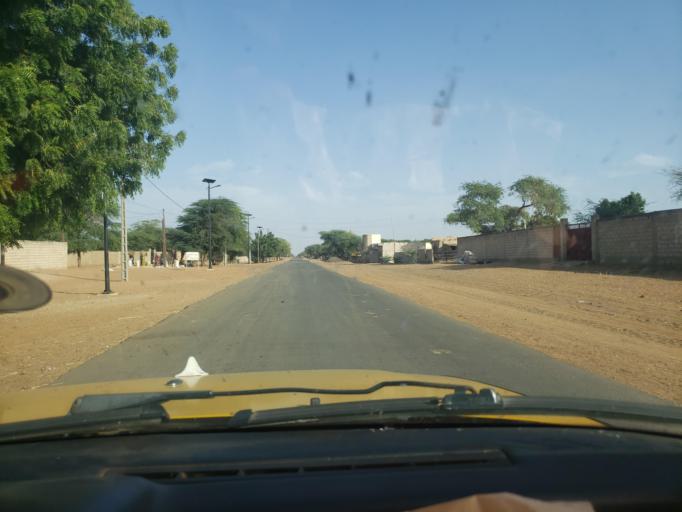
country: SN
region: Louga
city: Louga
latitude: 15.5116
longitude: -15.9889
